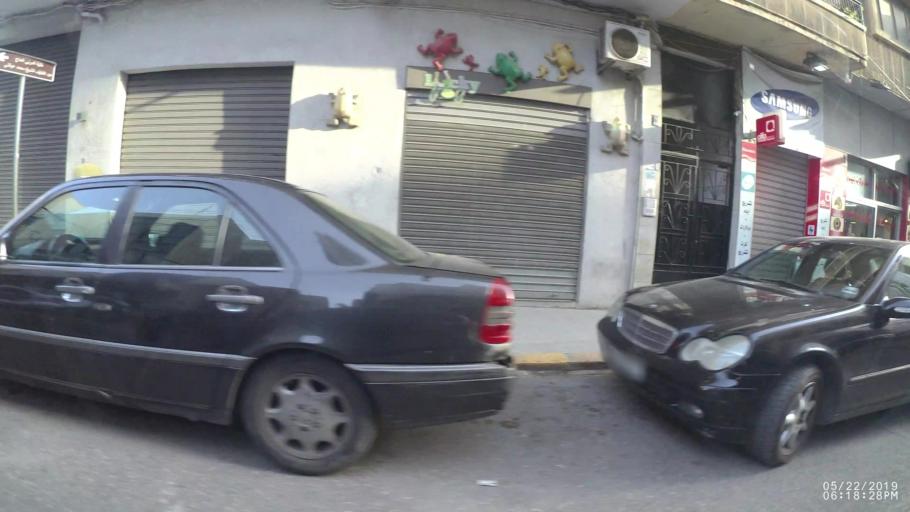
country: LB
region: Beyrouth
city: Ra's Bayrut
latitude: 33.8945
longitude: 35.4822
